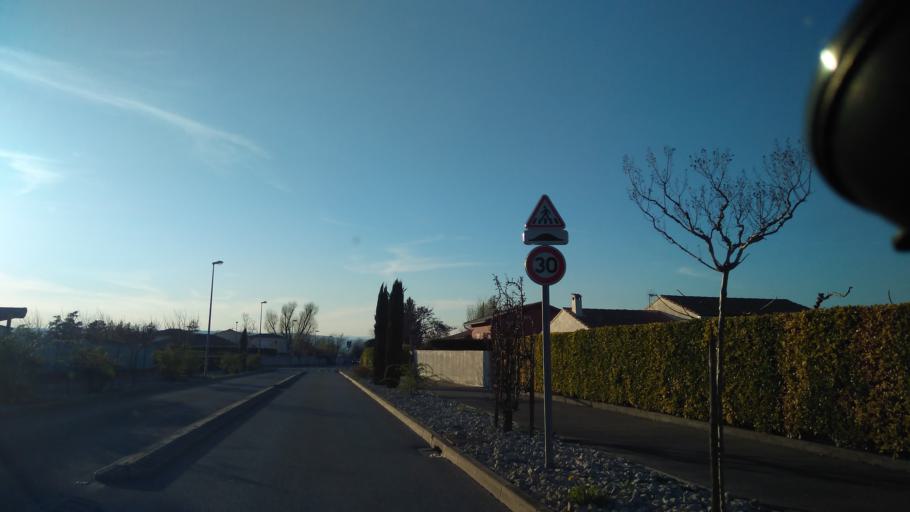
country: FR
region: Rhone-Alpes
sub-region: Departement de la Drome
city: Montelier
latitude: 44.9343
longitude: 5.0295
